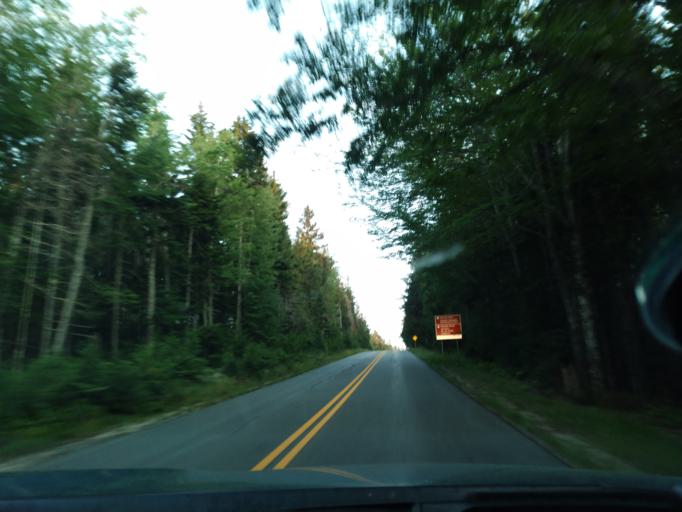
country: US
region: Maine
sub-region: Hancock County
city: Gouldsboro
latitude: 44.3828
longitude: -68.0690
